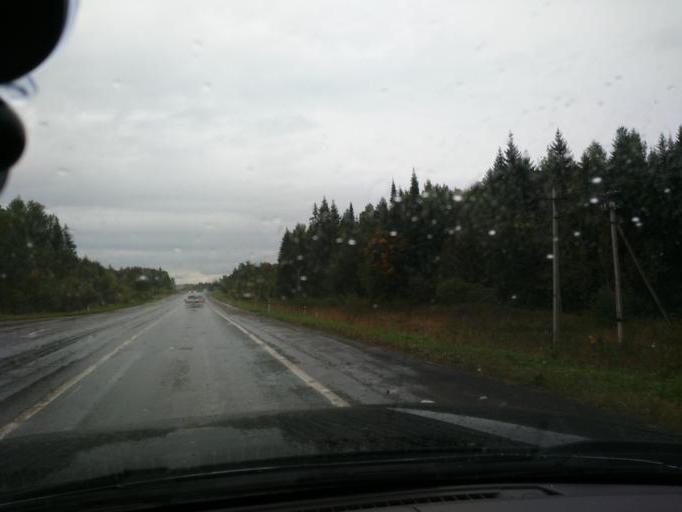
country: RU
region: Perm
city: Kultayevo
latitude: 57.8204
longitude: 55.8021
